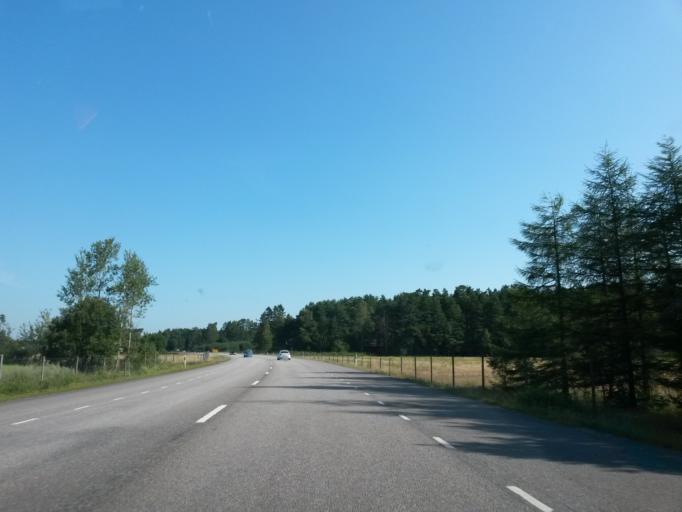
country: SE
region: Vaestra Goetaland
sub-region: Vara Kommun
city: Vara
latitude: 58.1907
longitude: 12.8996
